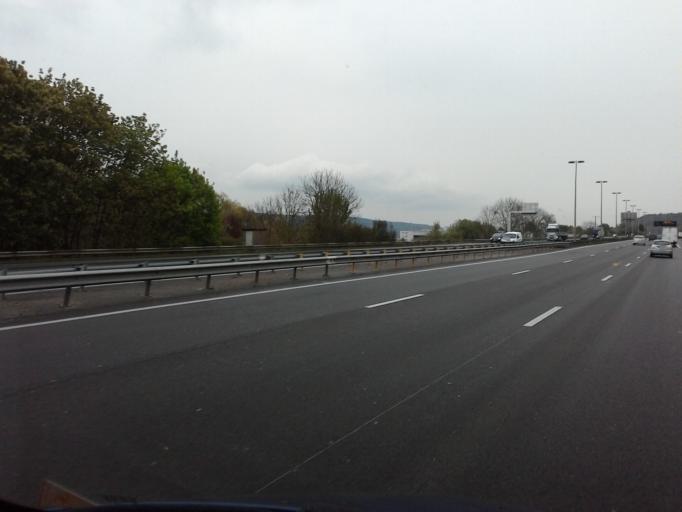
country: FR
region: Lorraine
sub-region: Departement de Meurthe-et-Moselle
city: Champigneulles
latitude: 48.7396
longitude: 6.1542
